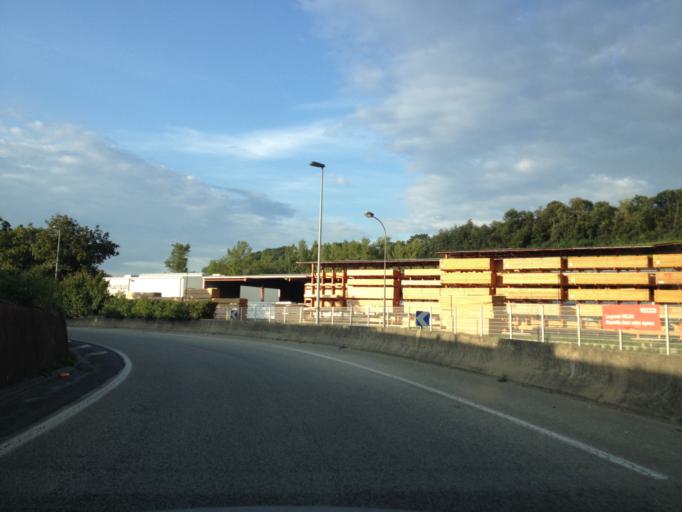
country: FR
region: Rhone-Alpes
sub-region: Departement de la Savoie
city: La Motte-Servolex
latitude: 45.6022
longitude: 5.8930
